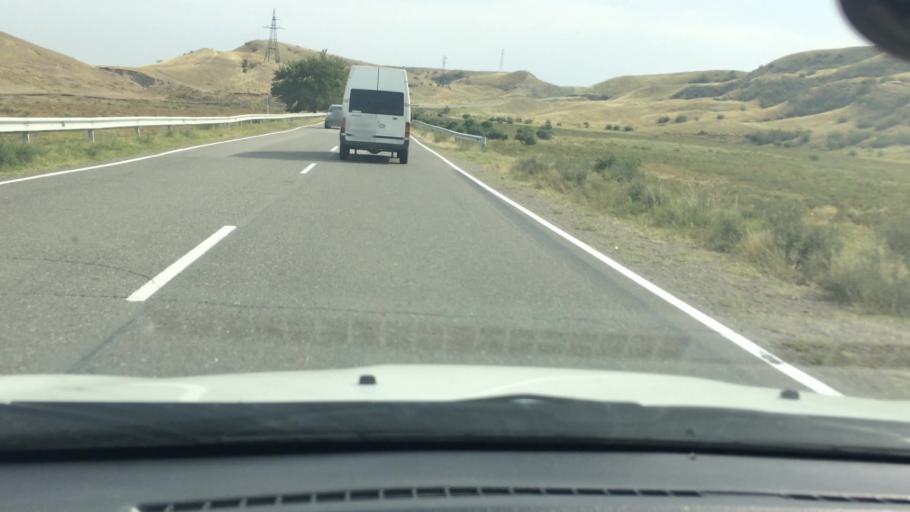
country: GE
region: Kvemo Kartli
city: Rust'avi
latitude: 41.5303
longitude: 44.9852
